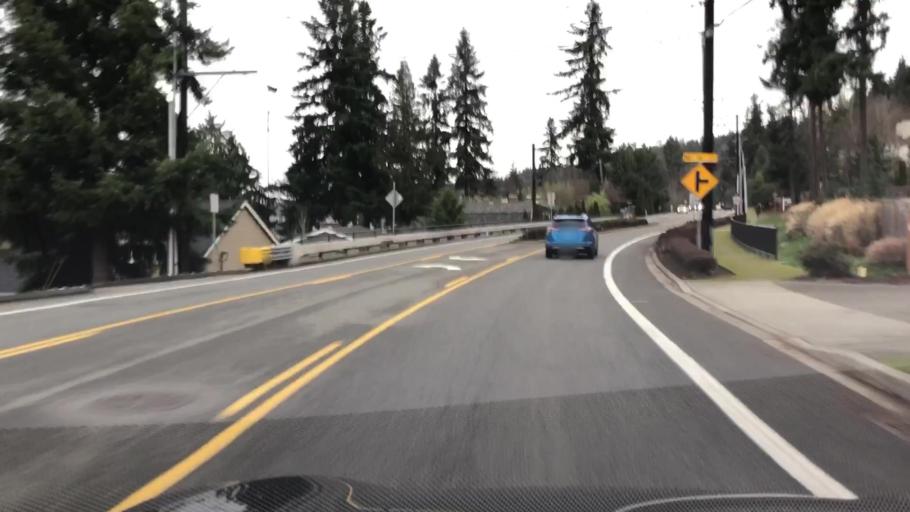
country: US
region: Washington
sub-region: King County
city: Sammamish
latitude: 47.6235
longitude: -122.0702
